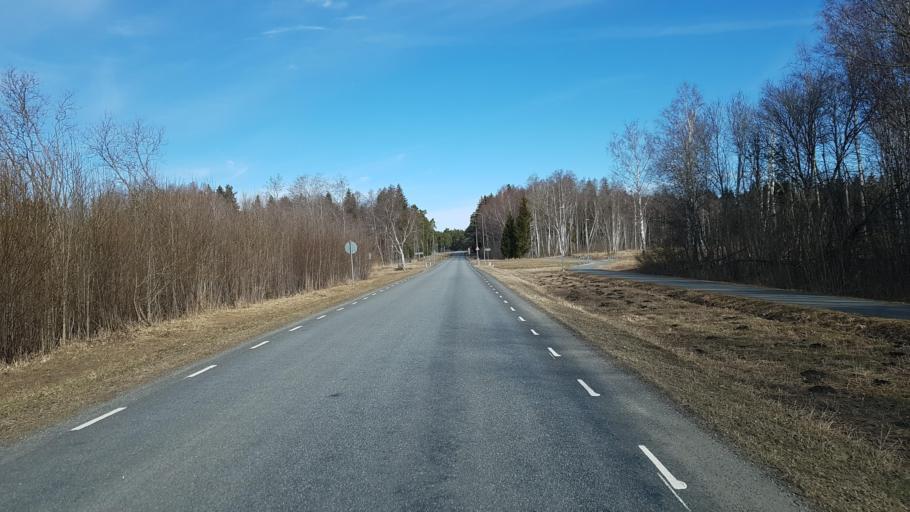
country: EE
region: Harju
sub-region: Nissi vald
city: Riisipere
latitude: 59.2422
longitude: 24.2437
